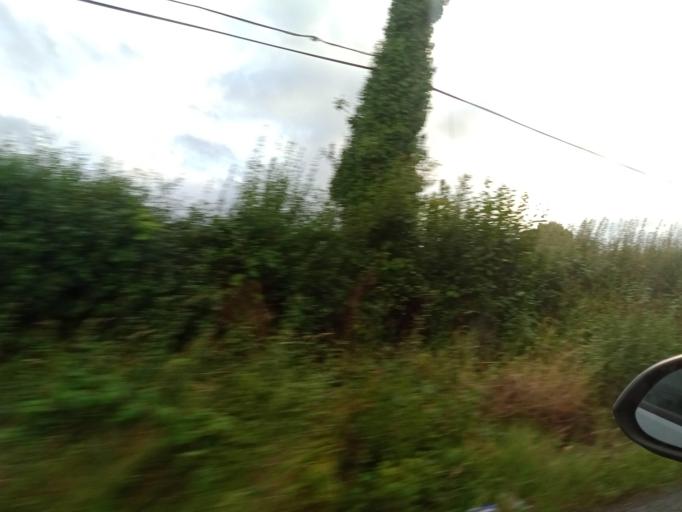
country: IE
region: Leinster
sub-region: Uibh Fhaili
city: Tullamore
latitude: 53.1450
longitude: -7.4790
